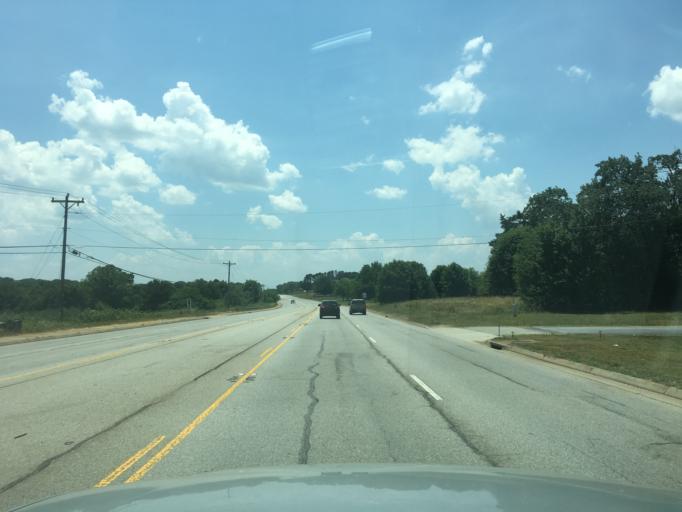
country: US
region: South Carolina
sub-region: Anderson County
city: Northlake
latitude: 34.5940
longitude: -82.6179
